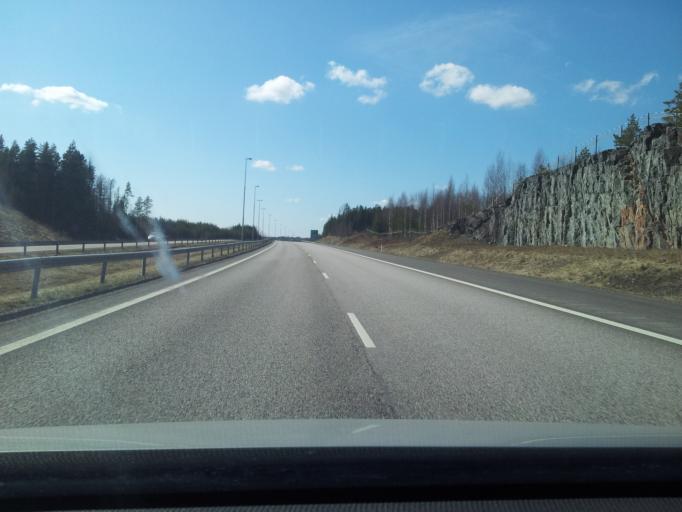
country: FI
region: Uusimaa
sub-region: Loviisa
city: Perna
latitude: 60.4908
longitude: 25.9931
